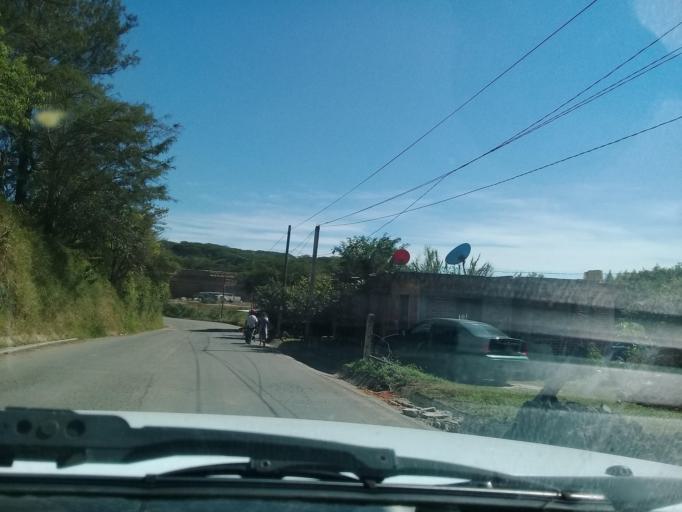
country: MX
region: Veracruz
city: El Castillo
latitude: 19.5488
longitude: -96.8504
